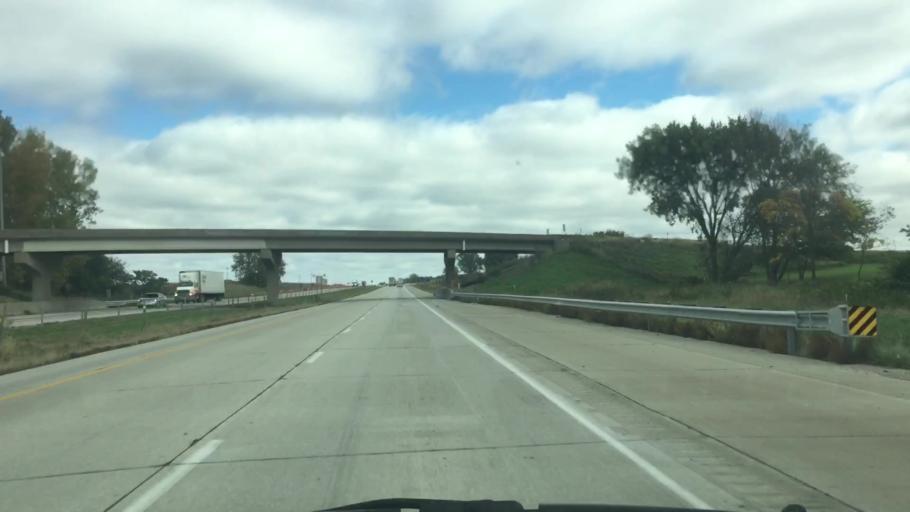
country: US
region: Iowa
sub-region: Polk County
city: Bondurant
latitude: 41.6716
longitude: -93.4450
